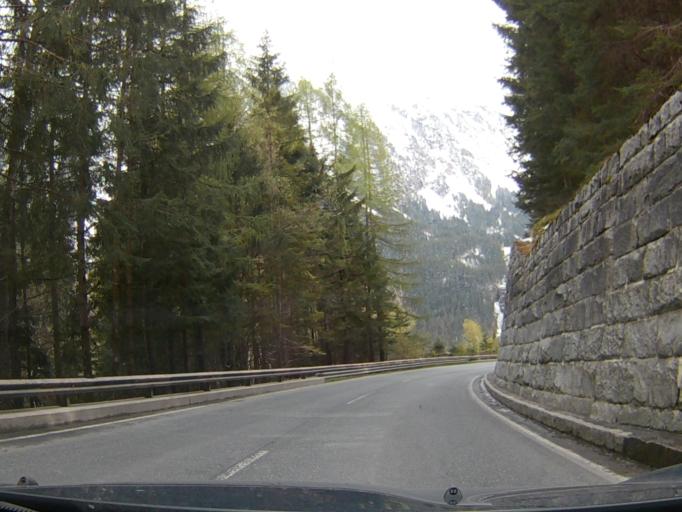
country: AT
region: Salzburg
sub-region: Politischer Bezirk Zell am See
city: Krimml
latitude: 47.2157
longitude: 12.1636
